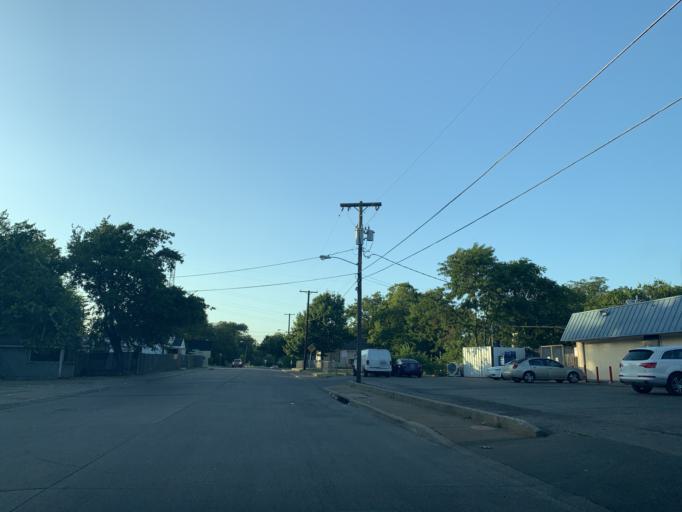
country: US
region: Texas
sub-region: Dallas County
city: Dallas
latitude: 32.7016
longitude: -96.8062
